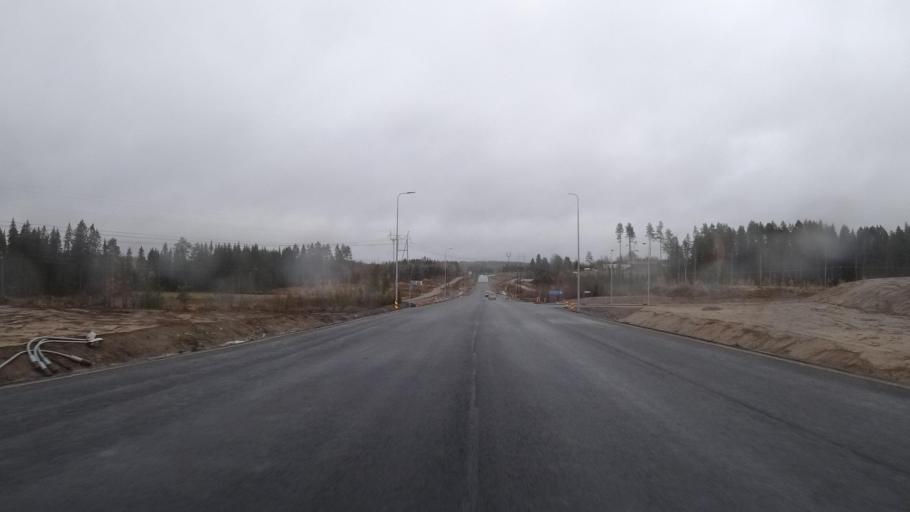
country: FI
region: Northern Savo
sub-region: Varkaus
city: Kangaslampi
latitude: 62.3979
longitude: 28.1538
